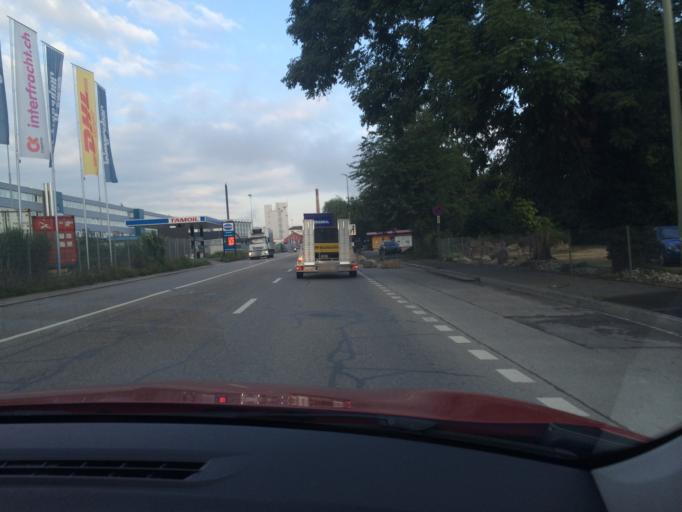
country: CH
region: Basel-Landschaft
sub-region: Bezirk Liestal
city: Pratteln
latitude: 47.5314
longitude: 7.6845
